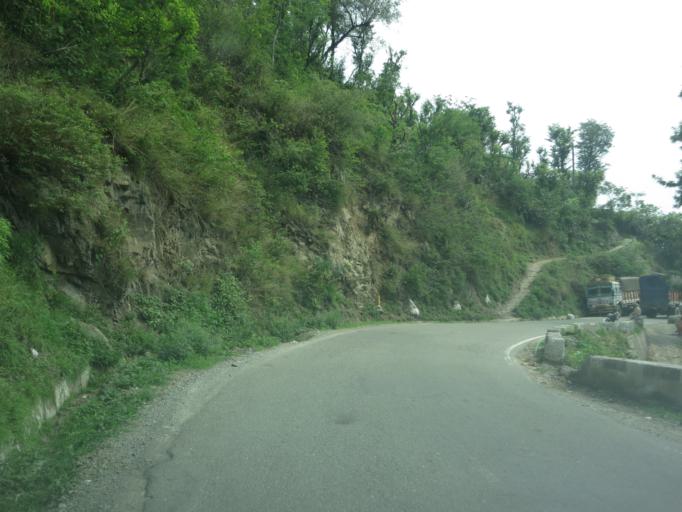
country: IN
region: Himachal Pradesh
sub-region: Solan
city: Arki
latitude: 31.2545
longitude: 76.8739
